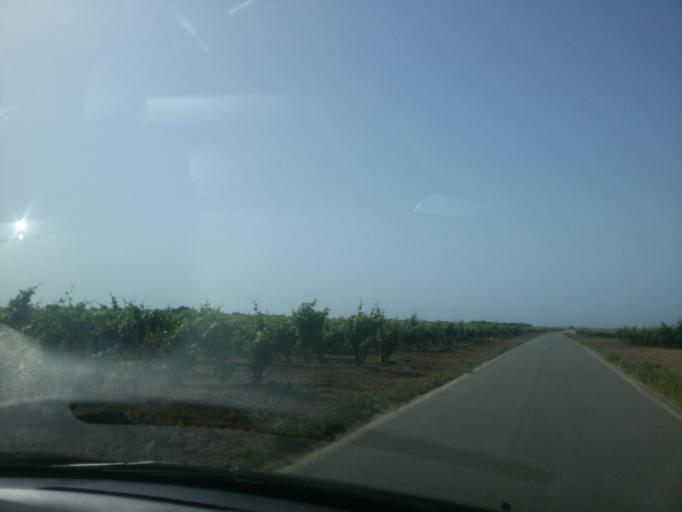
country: IT
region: Apulia
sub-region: Provincia di Brindisi
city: Brindisi
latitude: 40.6729
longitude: 17.8872
